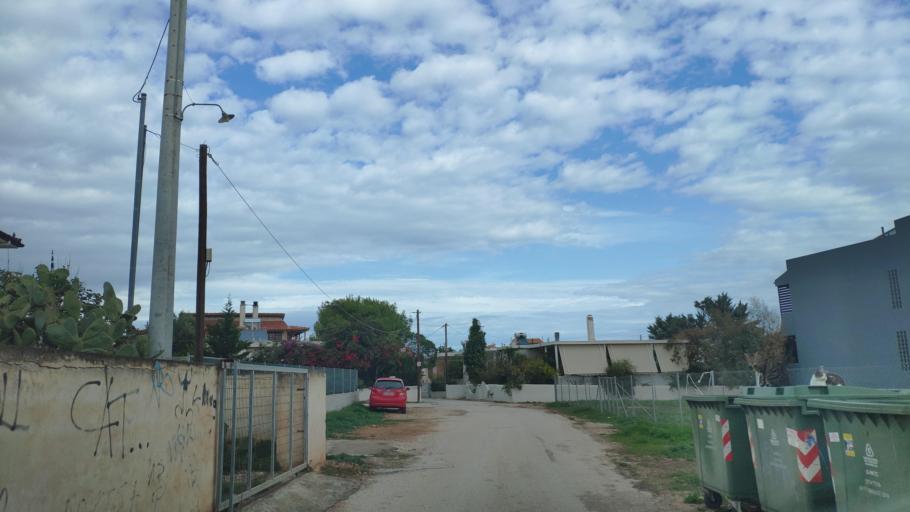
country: GR
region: Attica
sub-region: Nomarchia Anatolikis Attikis
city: Artemida
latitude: 37.9408
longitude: 24.0145
